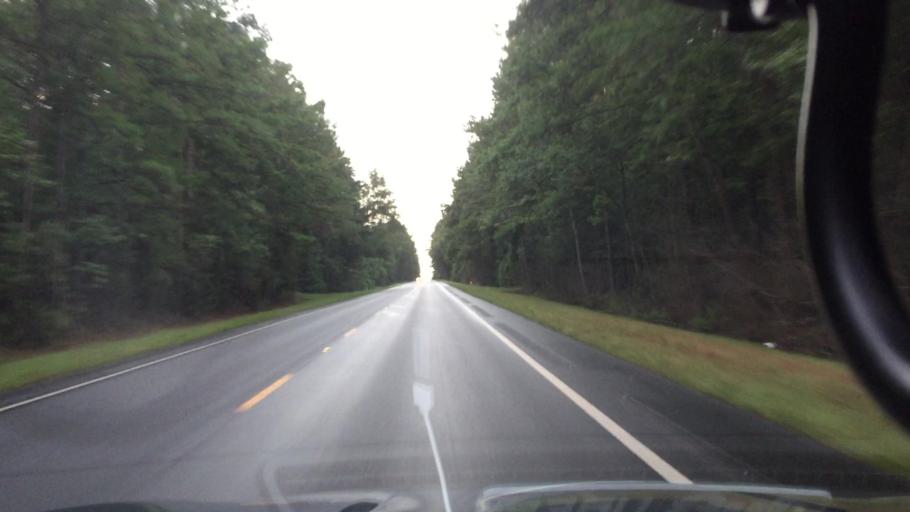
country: US
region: Alabama
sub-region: Coffee County
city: New Brockton
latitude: 31.4561
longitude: -85.8972
